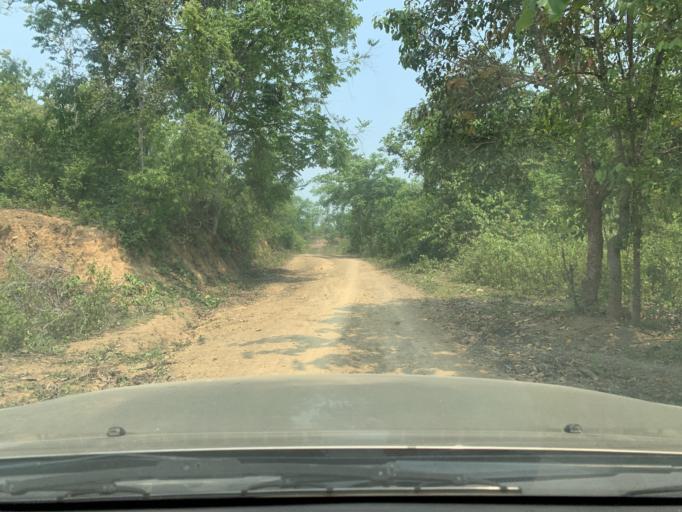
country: LA
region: Louangphabang
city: Louangphabang
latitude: 19.9421
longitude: 102.1332
